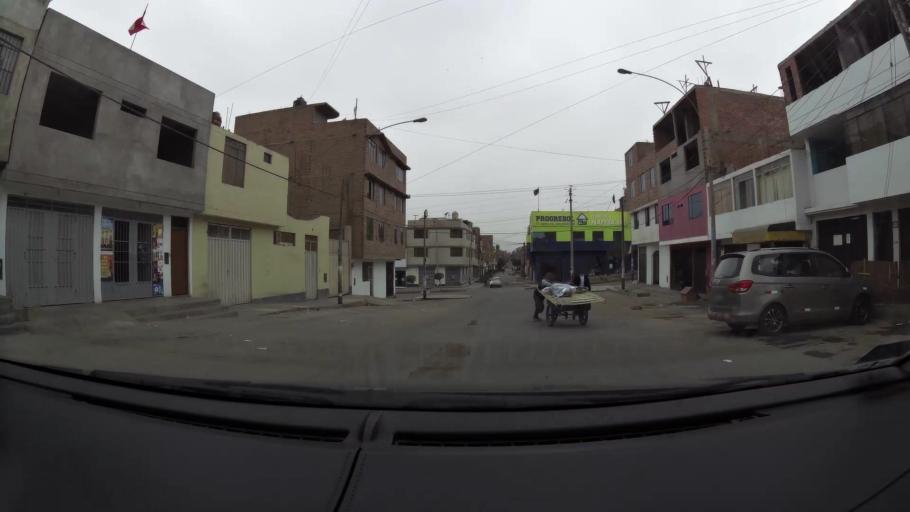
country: PE
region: Lima
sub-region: Lima
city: Independencia
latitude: -11.9461
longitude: -77.0866
